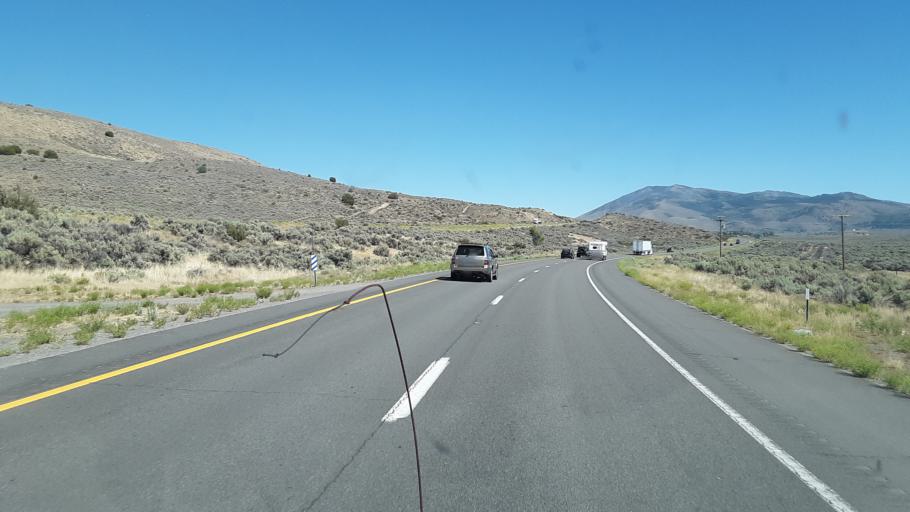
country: US
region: Nevada
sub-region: Washoe County
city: Cold Springs
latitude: 39.6902
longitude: -120.0158
